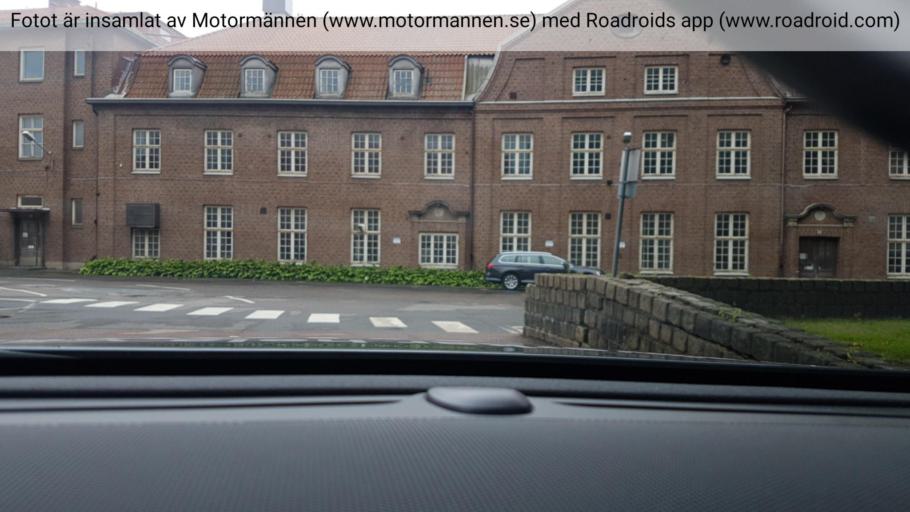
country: SE
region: Vaestra Goetaland
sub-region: Goteborg
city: Eriksbo
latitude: 57.7284
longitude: 12.0146
